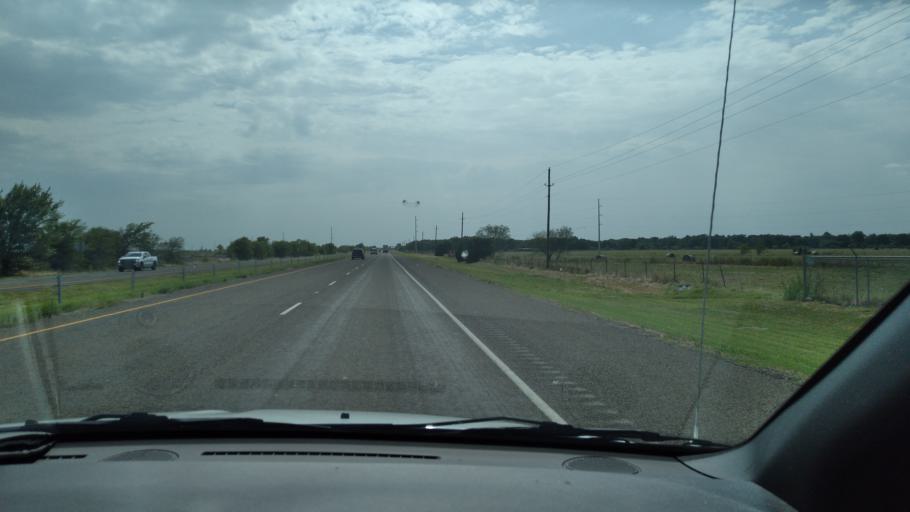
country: US
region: Texas
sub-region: Navarro County
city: Kerens
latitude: 32.1219
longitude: -96.2983
